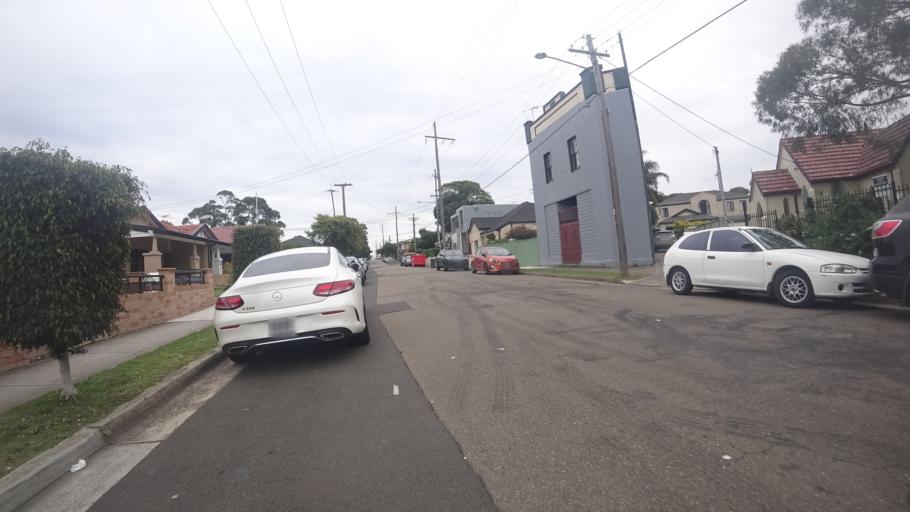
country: AU
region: New South Wales
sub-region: Rockdale
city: Arncliffe
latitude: -33.9335
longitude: 151.1435
